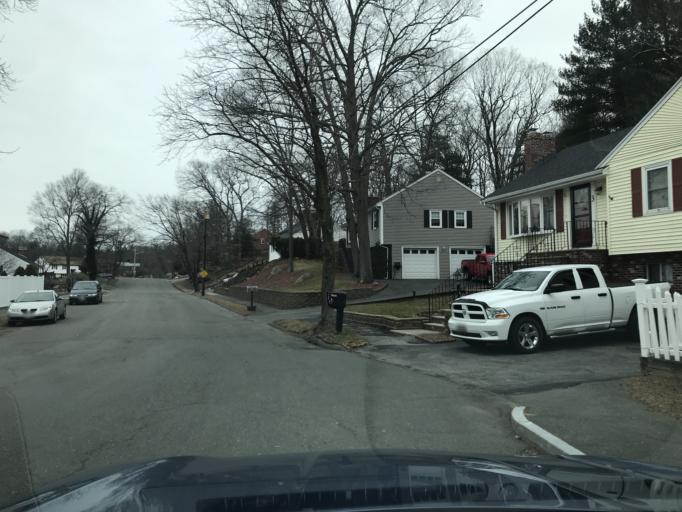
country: US
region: Massachusetts
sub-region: Essex County
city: Saugus
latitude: 42.4971
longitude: -71.0269
